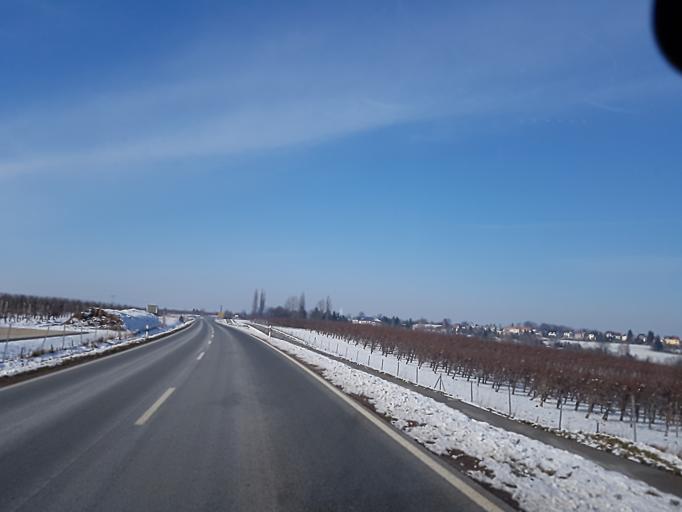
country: DE
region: Saxony
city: Leisnig
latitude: 51.1456
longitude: 12.9370
